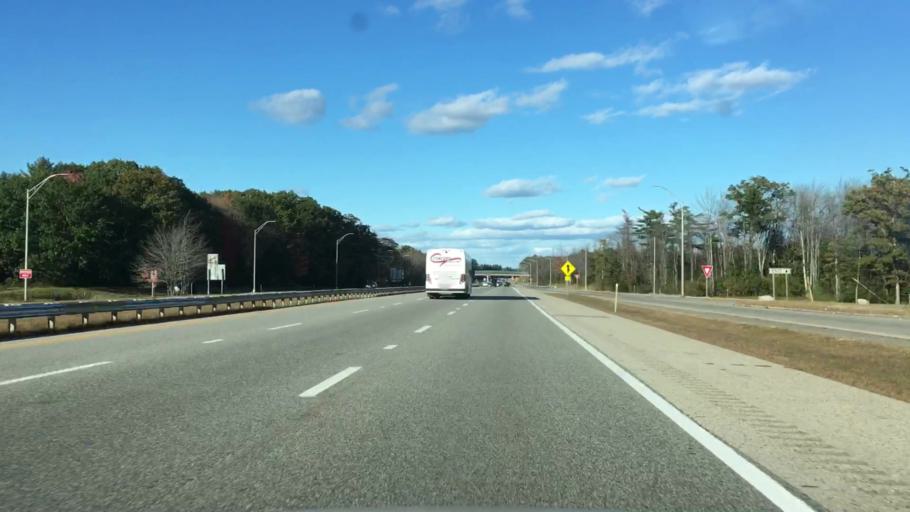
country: US
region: Maine
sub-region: York County
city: West Kennebunk
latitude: 43.4117
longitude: -70.5587
